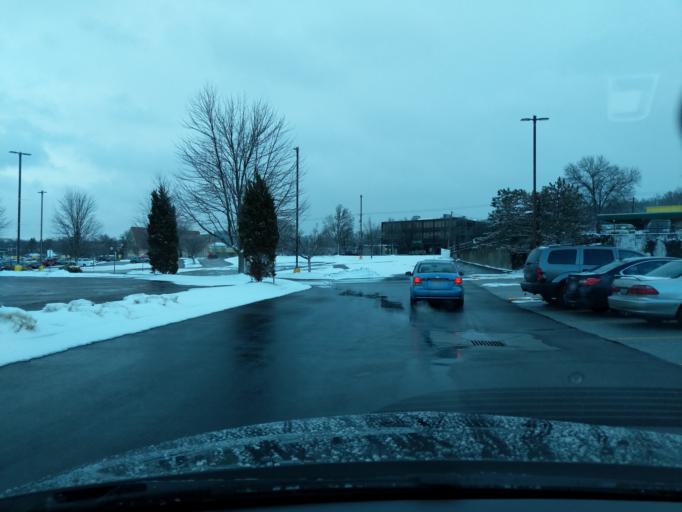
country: US
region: Ohio
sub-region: Summit County
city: Fairlawn
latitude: 41.1265
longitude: -81.6037
